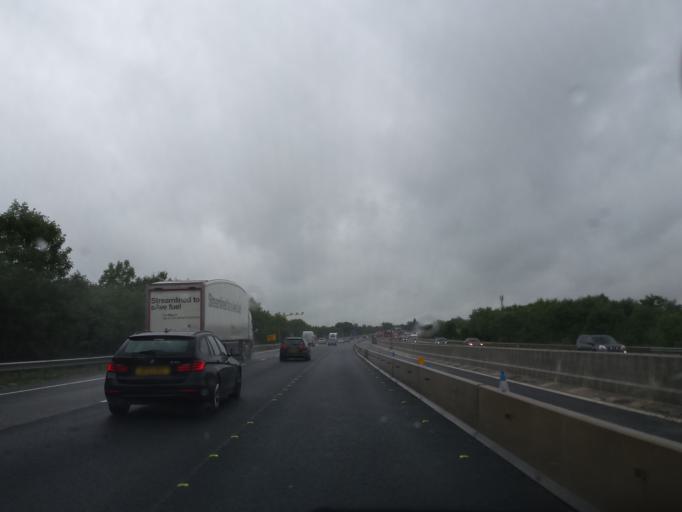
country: GB
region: England
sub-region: Rotherham
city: Harthill
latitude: 53.3234
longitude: -1.2809
